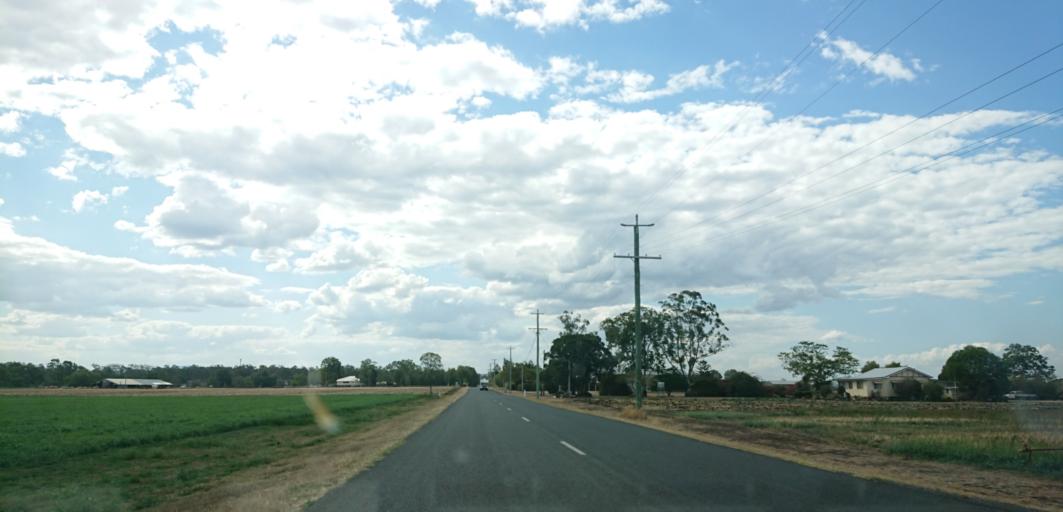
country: AU
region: Queensland
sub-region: Lockyer Valley
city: Gatton
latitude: -27.6134
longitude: 152.2086
